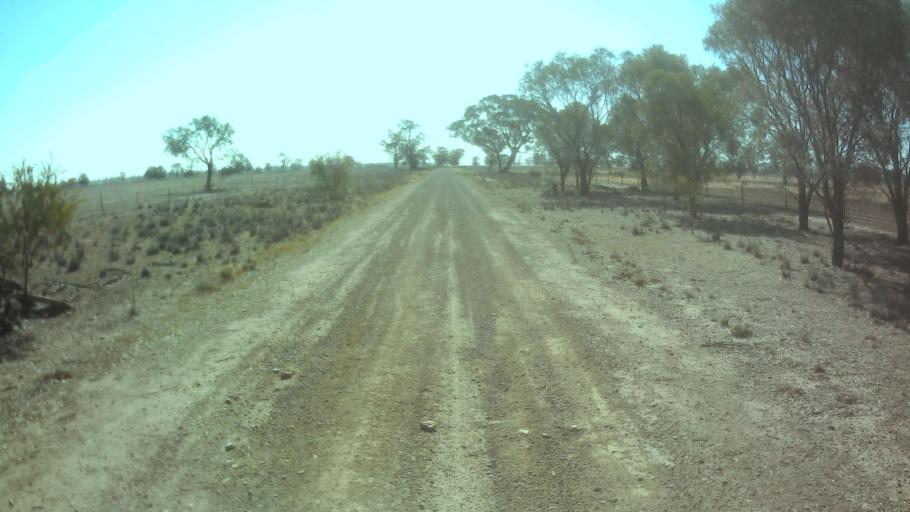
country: AU
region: New South Wales
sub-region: Forbes
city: Forbes
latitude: -33.7586
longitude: 147.6987
